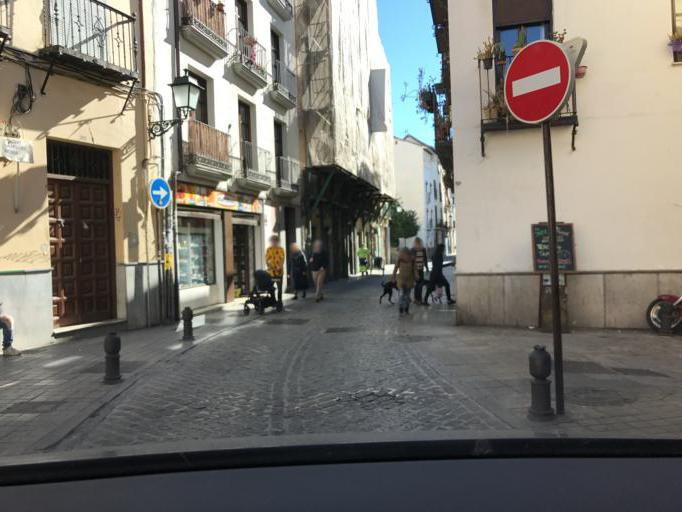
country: ES
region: Andalusia
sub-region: Provincia de Granada
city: Granada
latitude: 37.1819
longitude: -3.5993
